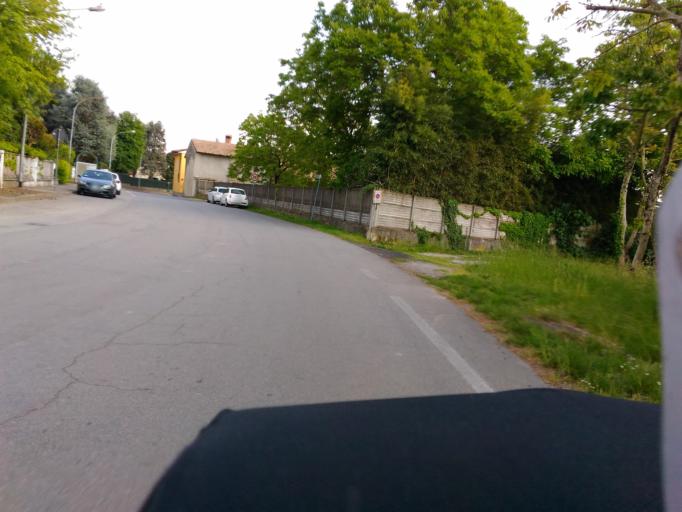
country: IT
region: Lombardy
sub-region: Citta metropolitana di Milano
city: Tribiano
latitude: 45.3953
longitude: 9.3716
